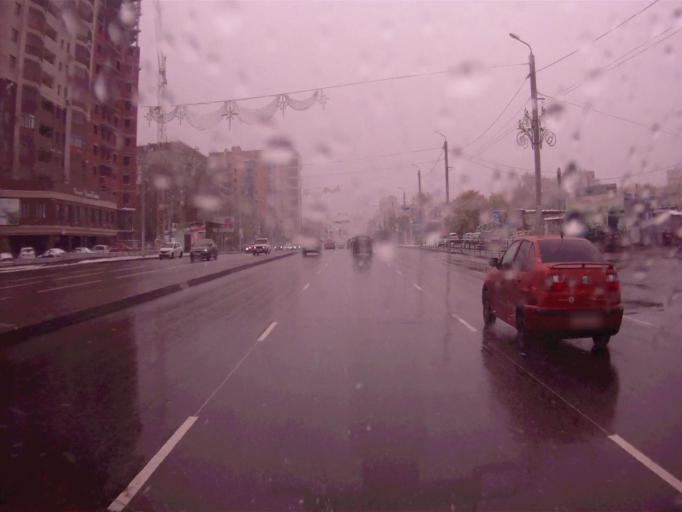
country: RU
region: Chelyabinsk
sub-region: Gorod Chelyabinsk
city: Chelyabinsk
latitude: 55.1455
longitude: 61.4008
